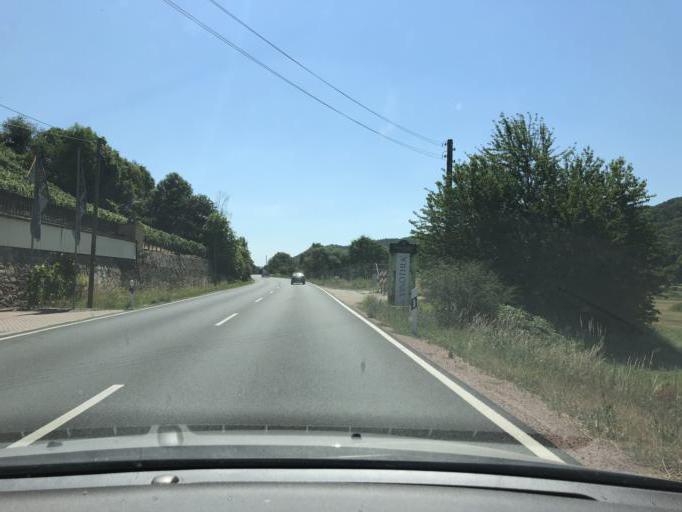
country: DE
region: Saxony
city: Meissen
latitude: 51.1408
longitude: 13.5045
